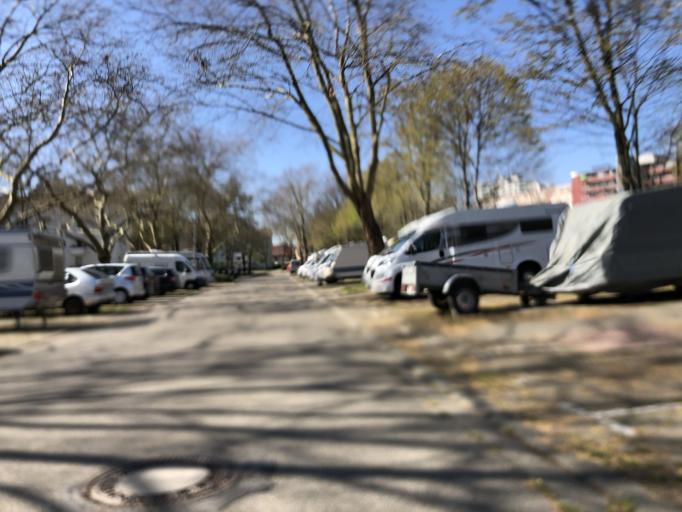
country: DE
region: Baden-Wuerttemberg
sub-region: Freiburg Region
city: Merzhausen
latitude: 47.9961
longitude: 7.8191
